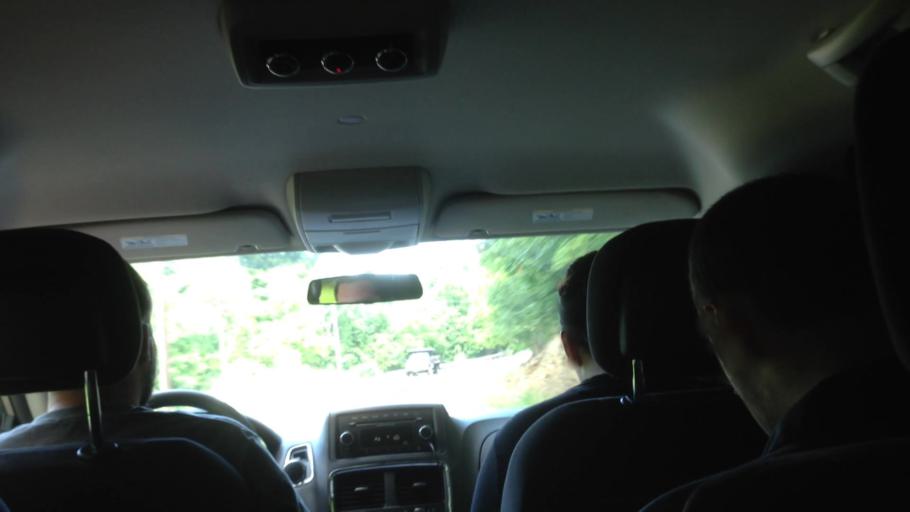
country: US
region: New York
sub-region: Dutchess County
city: Red Hook
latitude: 42.0164
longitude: -73.8527
